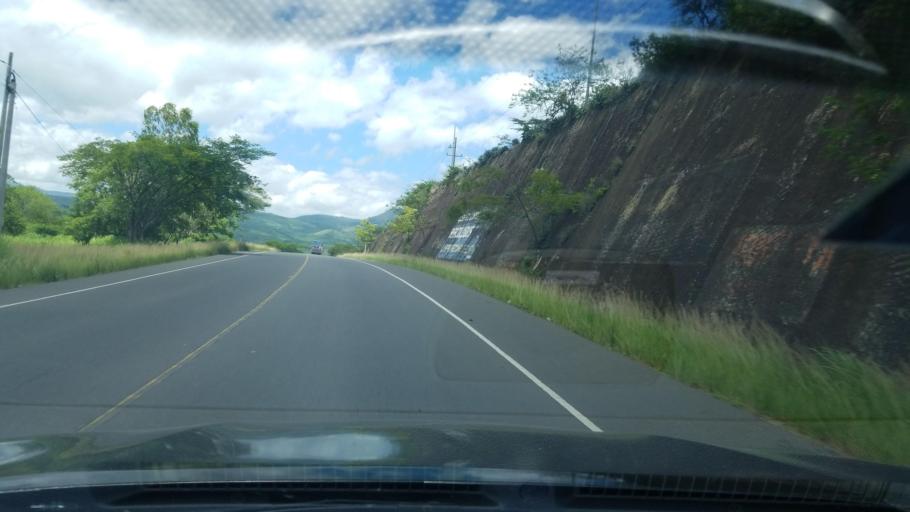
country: HN
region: Francisco Morazan
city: Cofradia
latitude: 14.2824
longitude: -87.2440
